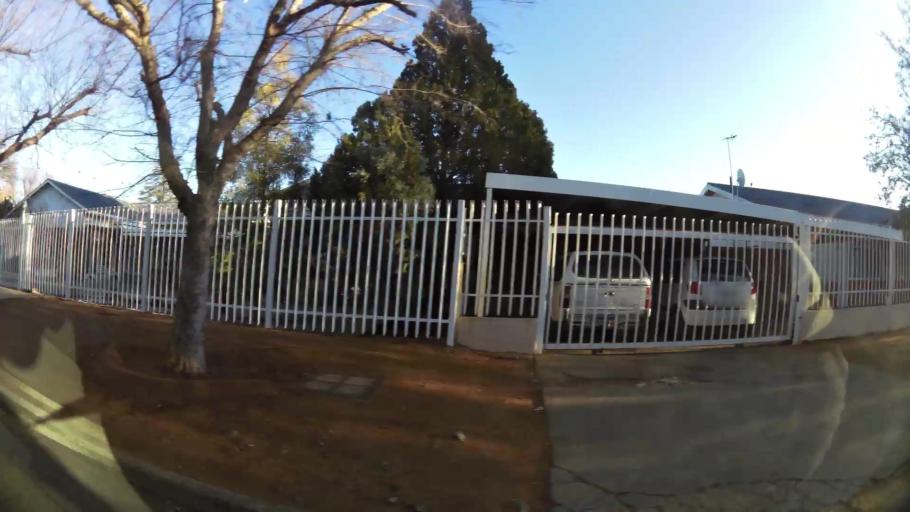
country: ZA
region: Northern Cape
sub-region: Frances Baard District Municipality
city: Kimberley
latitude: -28.7511
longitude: 24.7434
